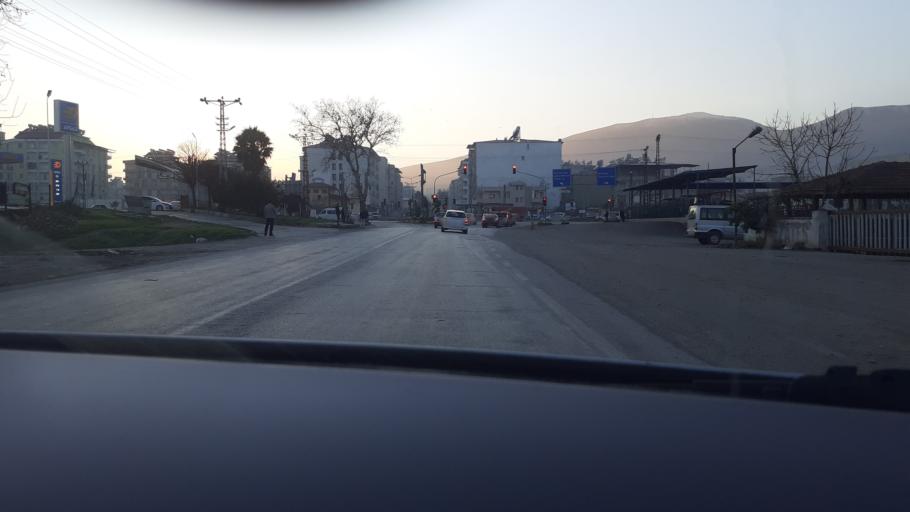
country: TR
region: Hatay
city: Kirikhan
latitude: 36.5003
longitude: 36.3746
